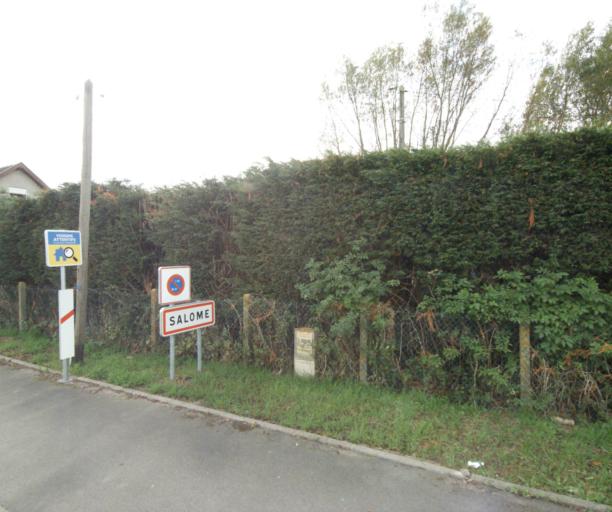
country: FR
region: Nord-Pas-de-Calais
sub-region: Departement du Nord
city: Salome
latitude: 50.5423
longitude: 2.8381
